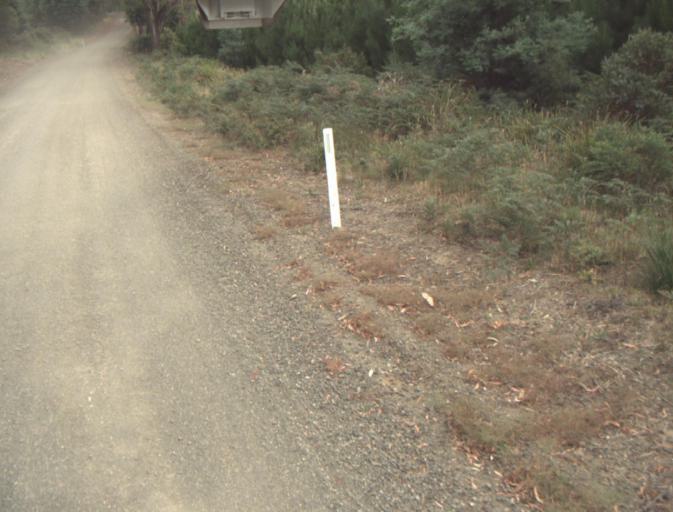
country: AU
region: Tasmania
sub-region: Dorset
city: Scottsdale
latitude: -41.4543
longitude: 147.5290
